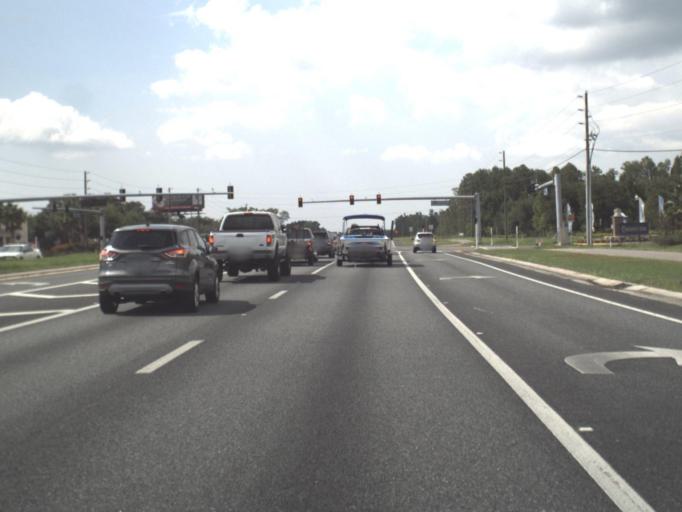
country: US
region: Florida
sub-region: Pasco County
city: Land O' Lakes
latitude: 28.2717
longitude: -82.4808
